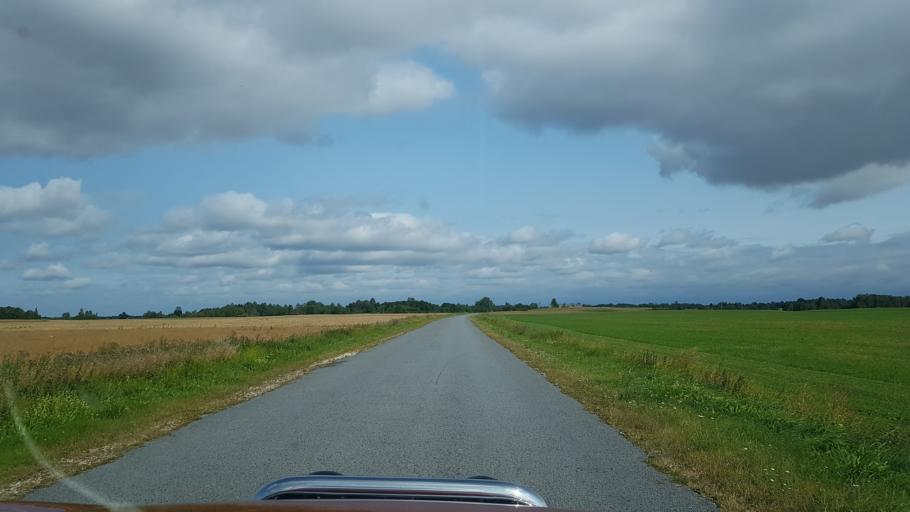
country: EE
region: Laeaene-Virumaa
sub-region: Kadrina vald
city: Kadrina
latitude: 59.3397
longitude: 26.0694
